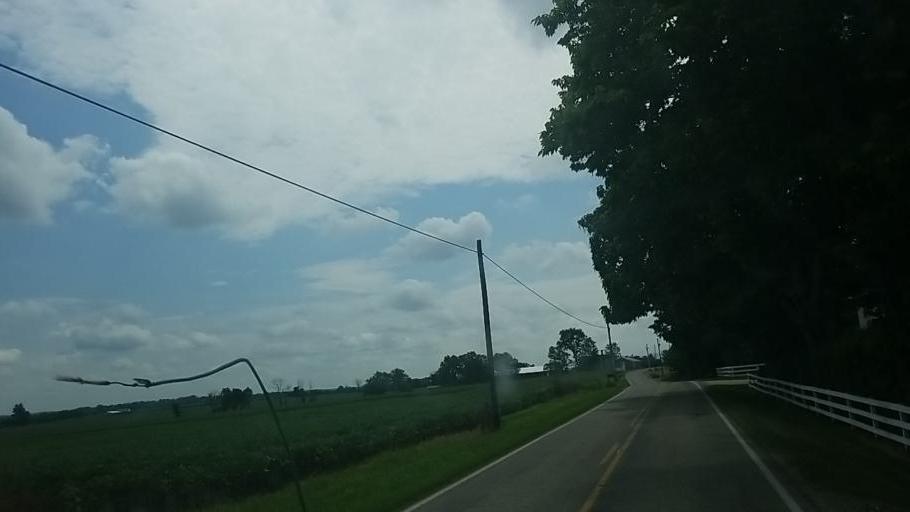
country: US
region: Ohio
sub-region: Pickaway County
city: Ashville
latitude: 39.7492
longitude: -82.8800
